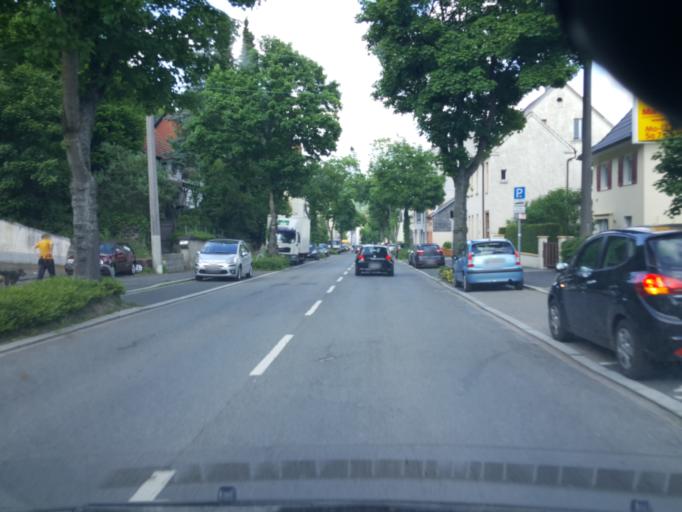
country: DE
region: North Rhine-Westphalia
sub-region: Regierungsbezirk Arnsberg
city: Hagen
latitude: 51.3413
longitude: 7.4851
